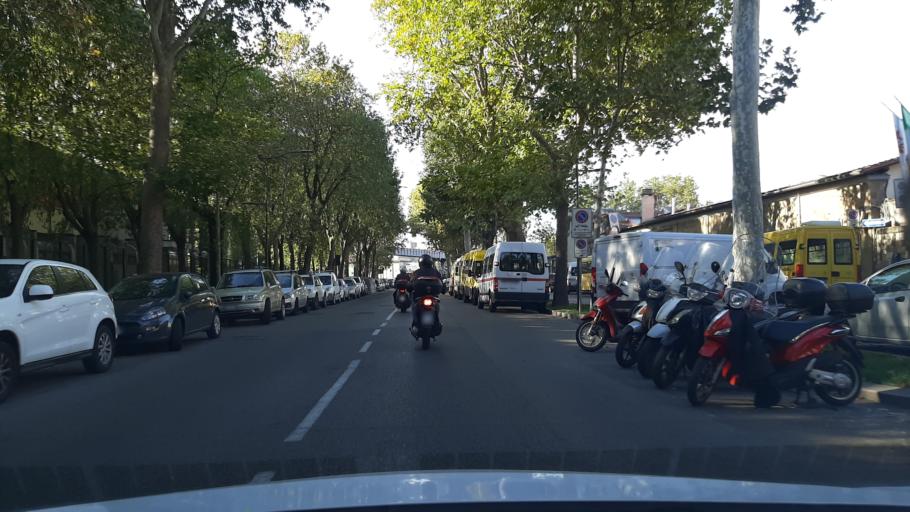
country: IT
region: Tuscany
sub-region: Province of Florence
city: Fiesole
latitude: 43.7790
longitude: 11.2796
